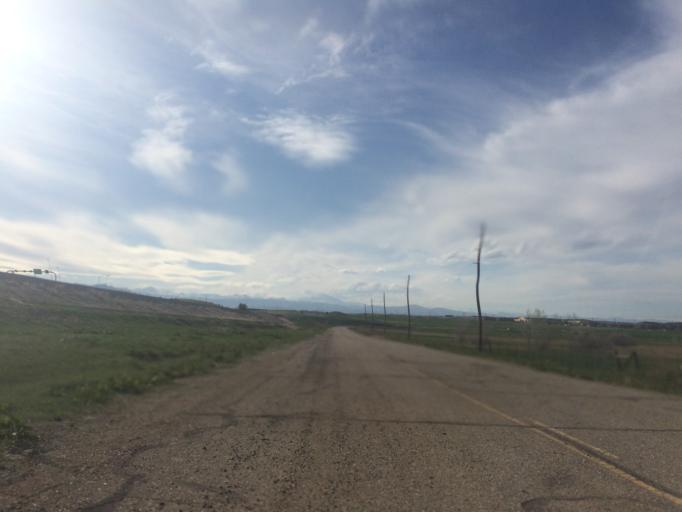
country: US
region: Colorado
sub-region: Broomfield County
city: Broomfield
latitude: 39.9306
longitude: -105.1155
